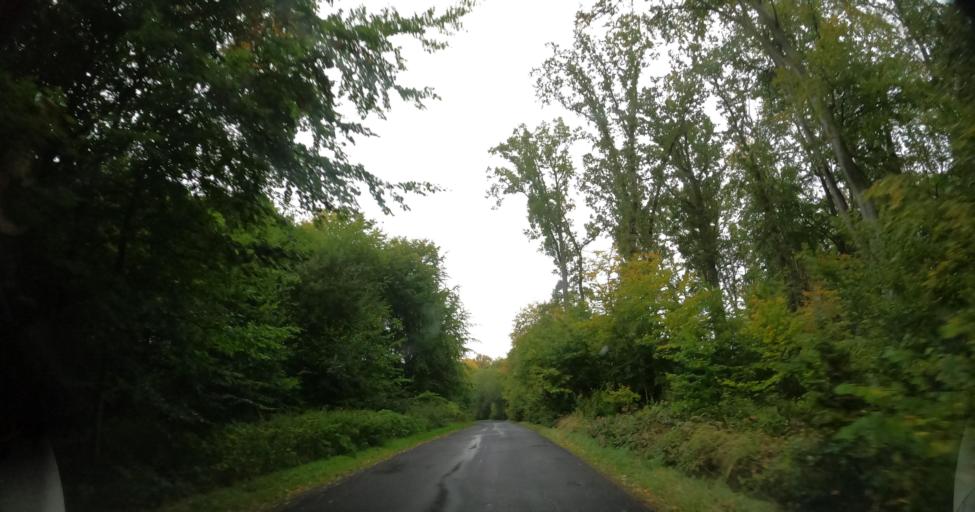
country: PL
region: West Pomeranian Voivodeship
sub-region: Powiat gryfinski
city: Banie
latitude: 53.0531
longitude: 14.7422
